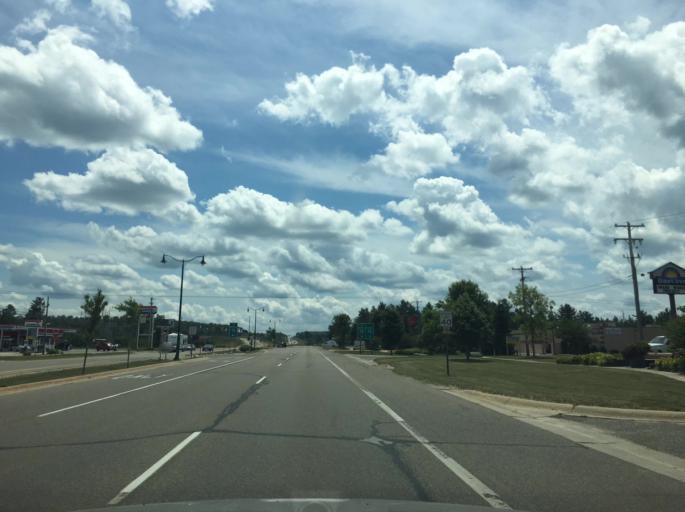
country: US
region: Michigan
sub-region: Crawford County
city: Grayling
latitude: 44.6490
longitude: -84.7088
